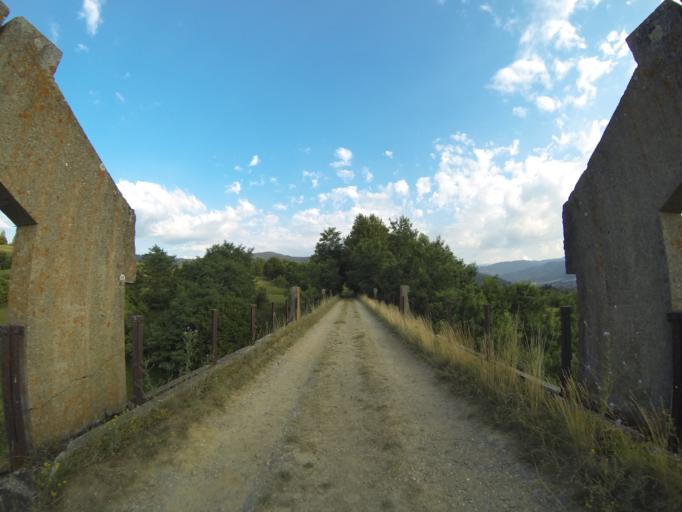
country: RO
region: Brasov
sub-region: Comuna Sinca Noua
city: Sinca Noua
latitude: 45.7161
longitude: 25.2518
